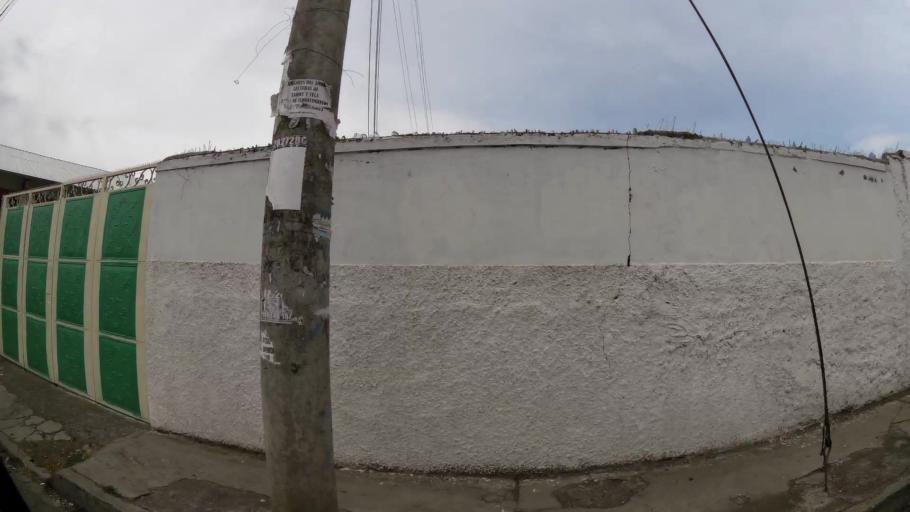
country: EC
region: Cotopaxi
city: Latacunga
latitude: -0.9347
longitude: -78.6107
